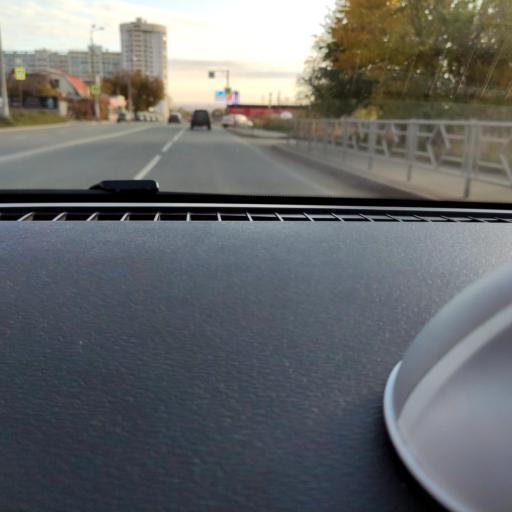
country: RU
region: Samara
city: Samara
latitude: 53.2052
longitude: 50.2098
